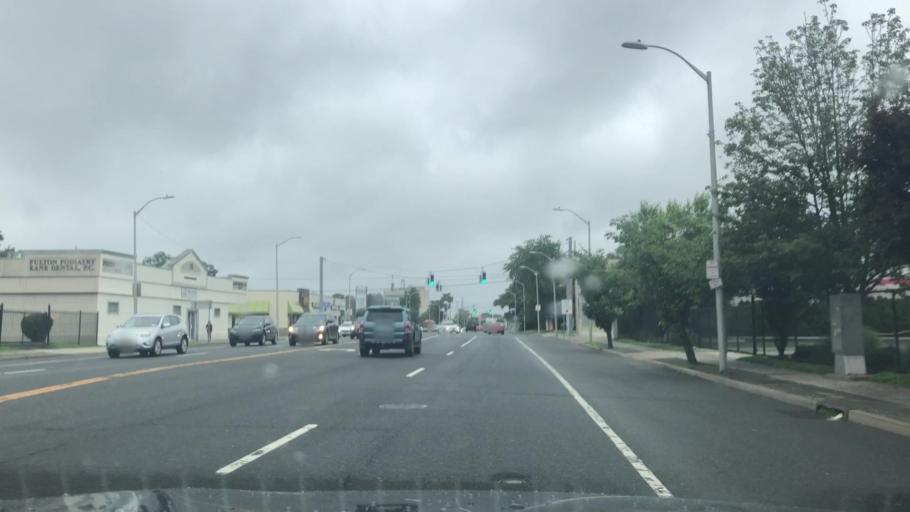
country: US
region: New York
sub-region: Nassau County
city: Hempstead
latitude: 40.7061
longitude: -73.6337
